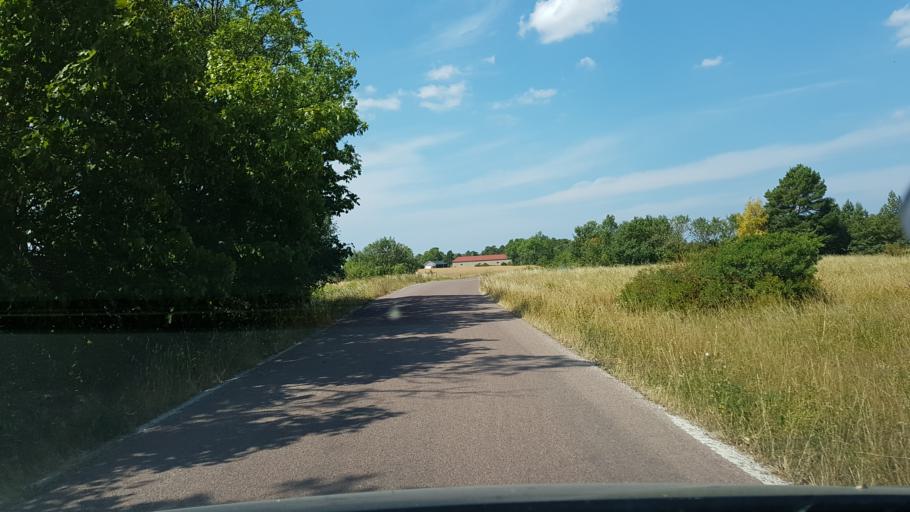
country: SE
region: Gotland
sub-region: Gotland
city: Visby
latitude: 57.6657
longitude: 18.3715
